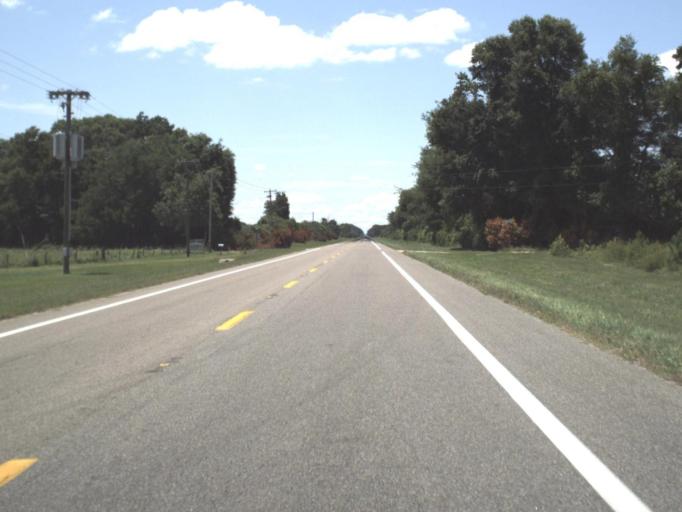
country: US
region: Florida
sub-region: Lafayette County
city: Mayo
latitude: 29.9983
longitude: -83.0176
